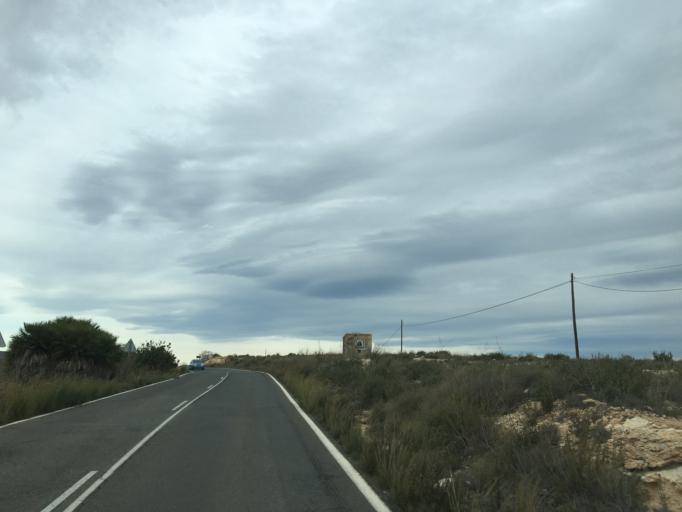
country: ES
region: Murcia
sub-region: Murcia
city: Cartagena
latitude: 37.6150
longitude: -1.0630
